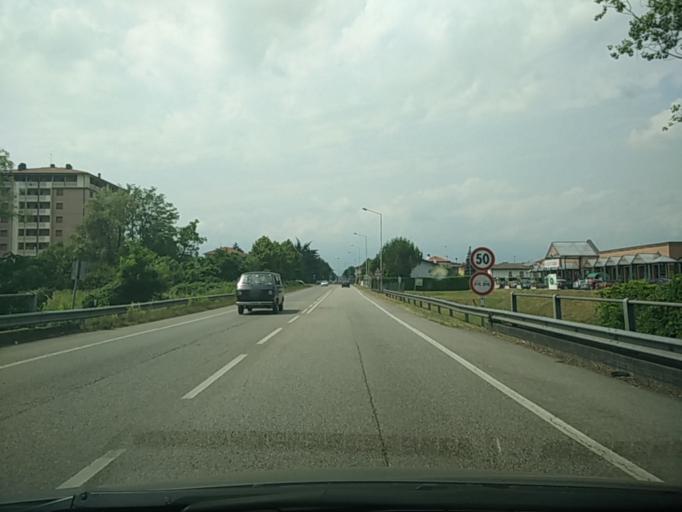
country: IT
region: Friuli Venezia Giulia
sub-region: Provincia di Pordenone
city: Pordenone
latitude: 45.9599
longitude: 12.6784
